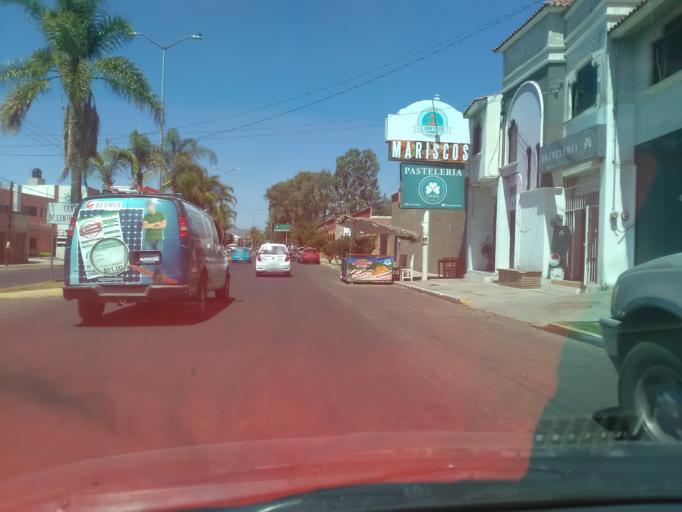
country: MX
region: Durango
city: Victoria de Durango
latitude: 24.0135
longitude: -104.6813
